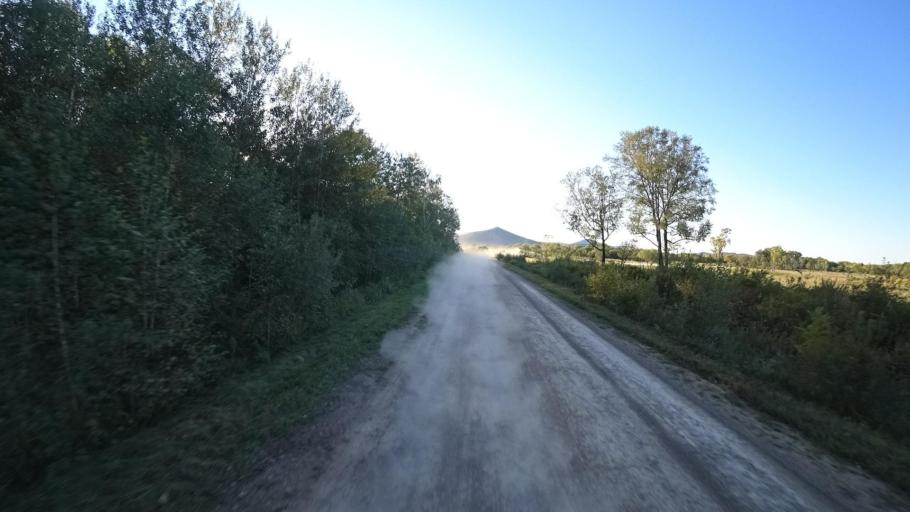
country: RU
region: Primorskiy
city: Kirovskiy
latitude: 44.8199
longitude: 133.6079
